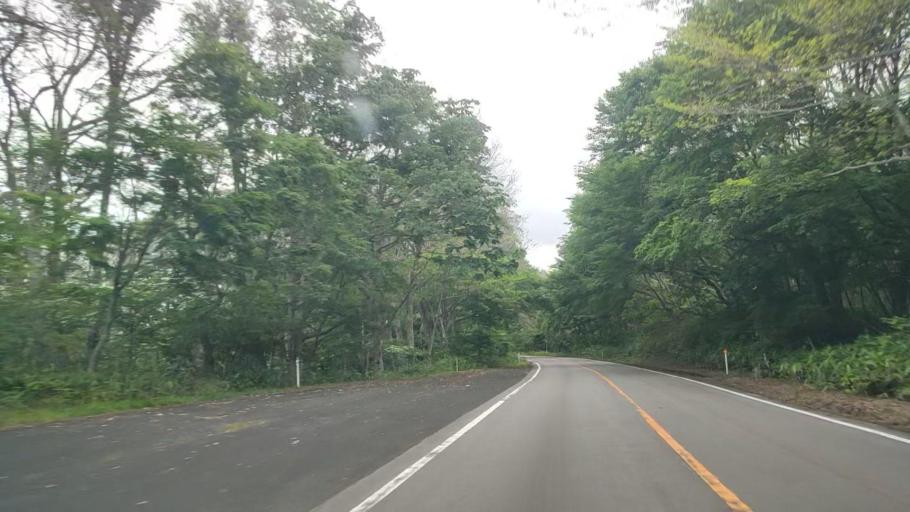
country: JP
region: Tottori
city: Kurayoshi
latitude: 35.3119
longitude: 133.6126
